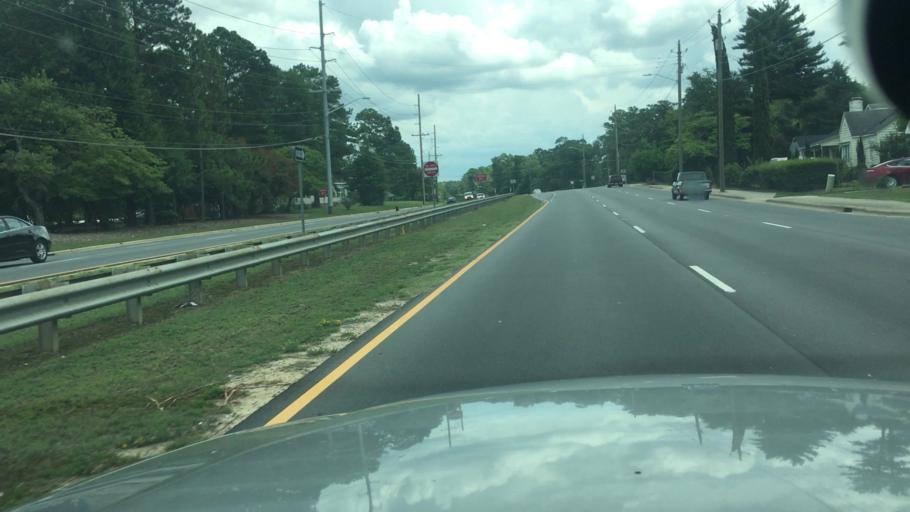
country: US
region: North Carolina
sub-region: Cumberland County
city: Fayetteville
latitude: 35.0705
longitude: -78.9191
